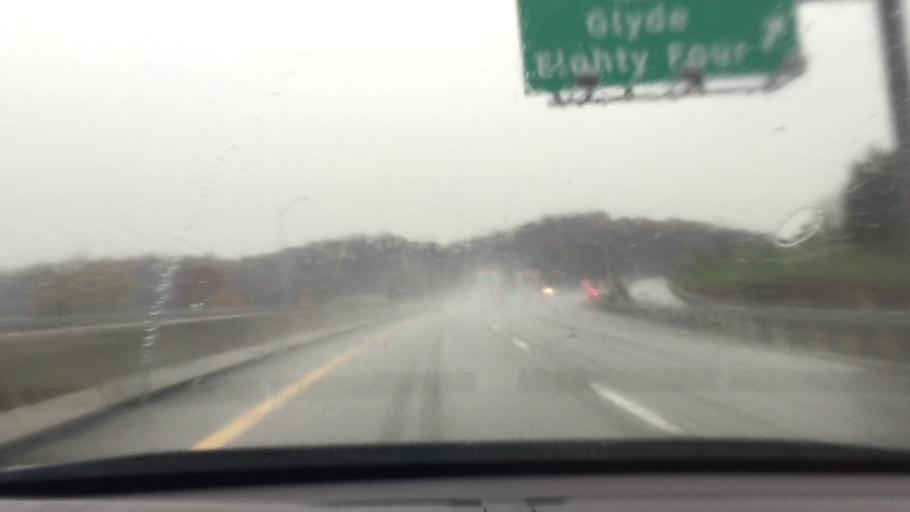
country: US
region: Pennsylvania
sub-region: Washington County
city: East Washington
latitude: 40.1558
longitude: -80.1248
